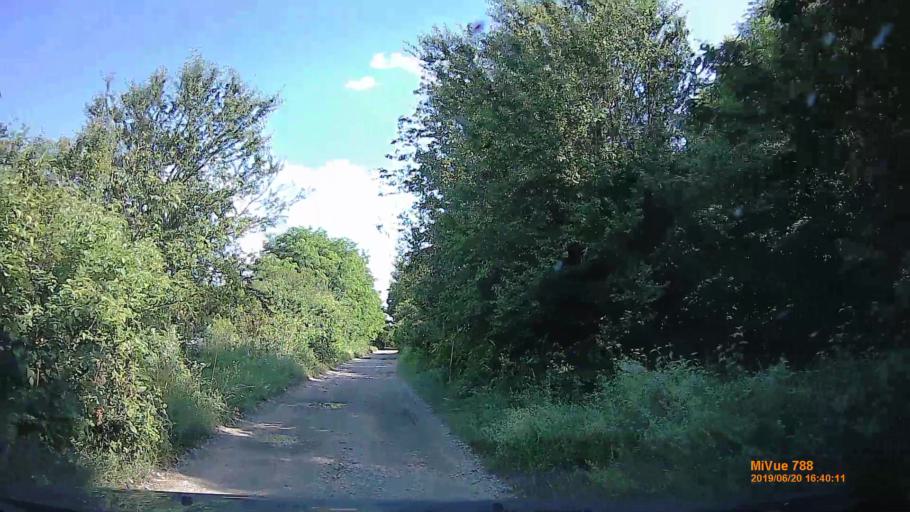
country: HU
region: Baranya
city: Buekkoesd
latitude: 46.1680
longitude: 18.0338
